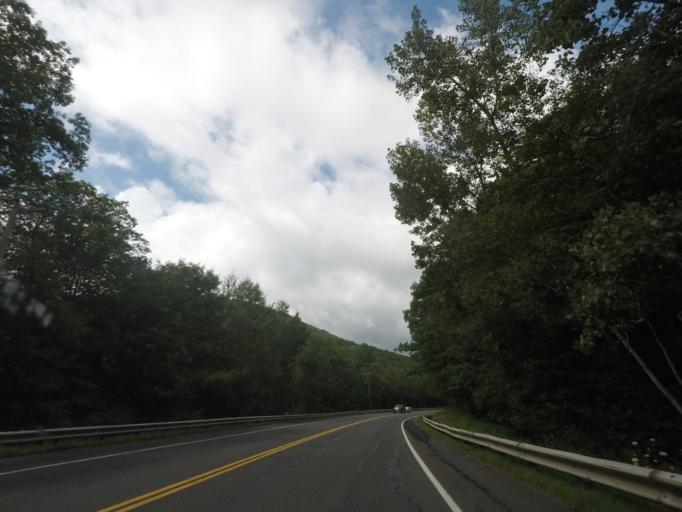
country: US
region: Massachusetts
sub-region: Berkshire County
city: Lanesborough
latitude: 42.5643
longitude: -73.2674
